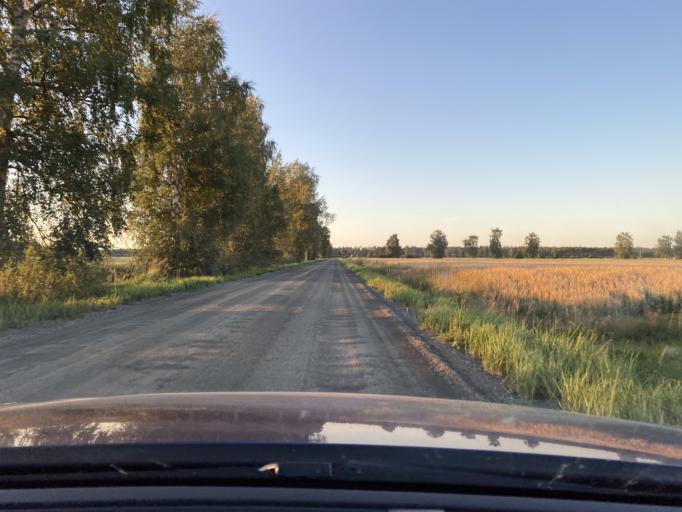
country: FI
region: Satakunta
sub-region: Rauma
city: Kiukainen
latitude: 61.1470
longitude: 22.0001
